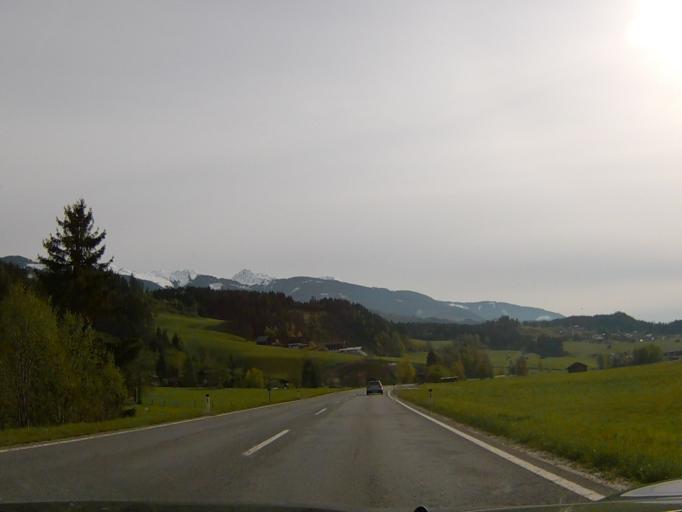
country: AT
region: Salzburg
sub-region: Politischer Bezirk Zell am See
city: Hollersbach im Pinzgau
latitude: 47.2786
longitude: 12.3866
